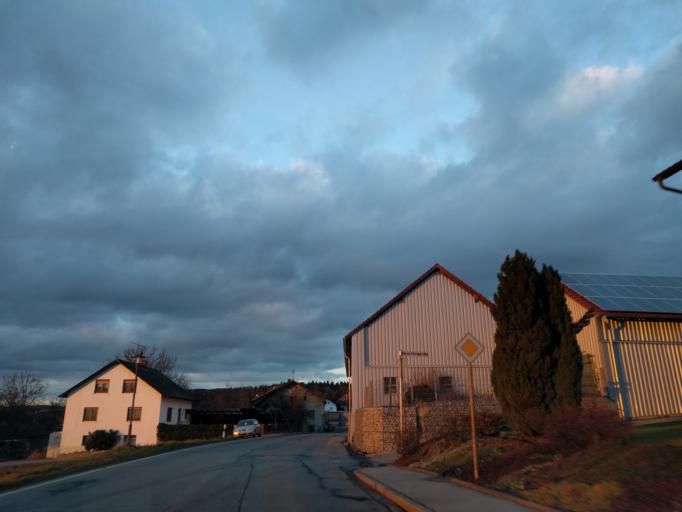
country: DE
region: Bavaria
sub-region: Lower Bavaria
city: Hofkirchen
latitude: 48.6921
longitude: 13.1211
